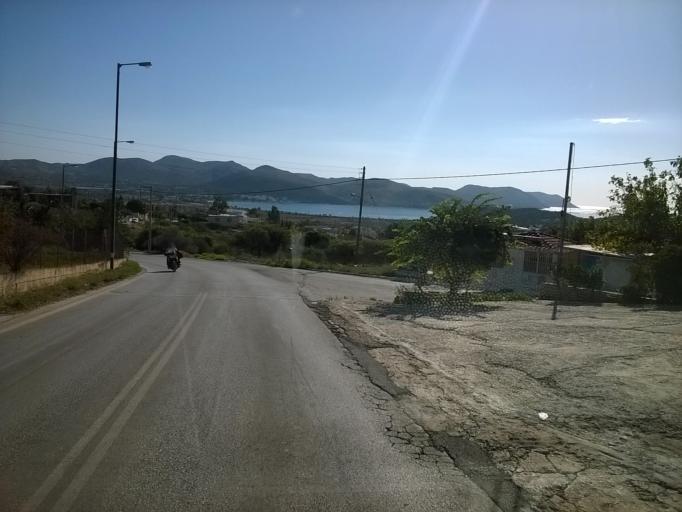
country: GR
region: Attica
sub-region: Nomarchia Anatolikis Attikis
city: Anavyssos
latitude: 37.7403
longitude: 23.9265
